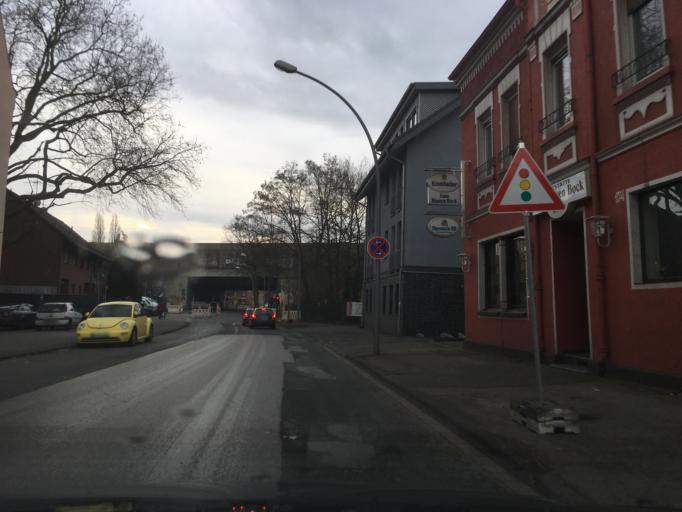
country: DE
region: North Rhine-Westphalia
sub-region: Regierungsbezirk Munster
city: Gladbeck
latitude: 51.5599
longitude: 7.0055
